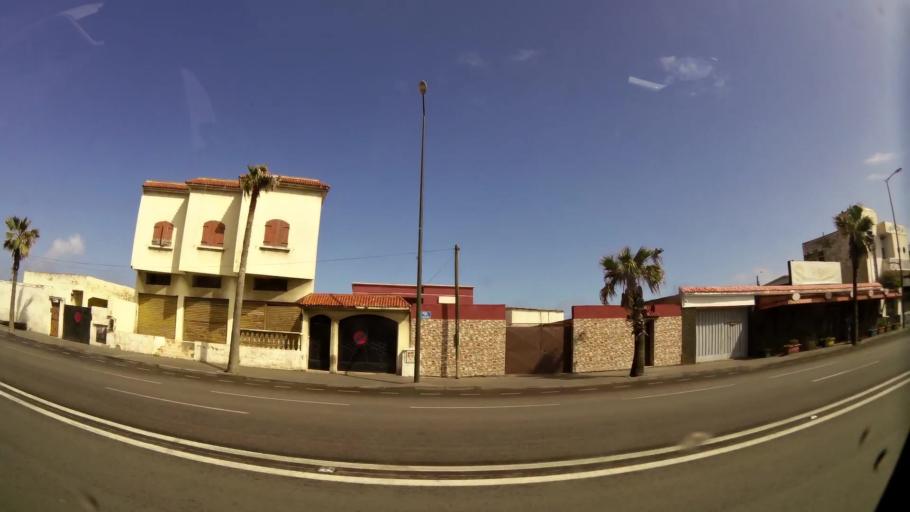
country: MA
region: Grand Casablanca
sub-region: Casablanca
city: Casablanca
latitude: 33.6190
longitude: -7.5387
